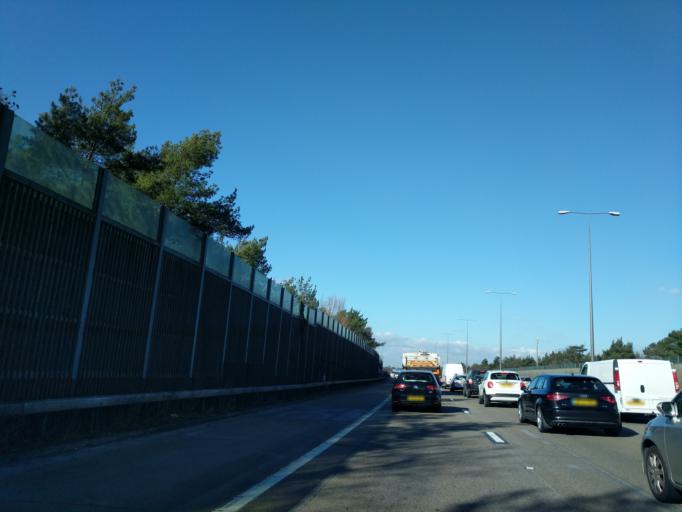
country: GB
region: England
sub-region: Surrey
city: Byfleet
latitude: 51.3502
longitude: -0.4875
